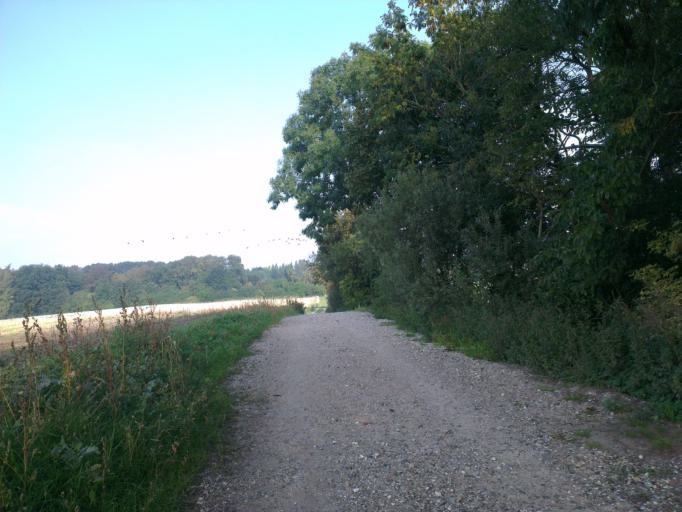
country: DK
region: Capital Region
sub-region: Frederikssund Kommune
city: Jaegerspris
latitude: 55.8600
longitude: 11.9948
